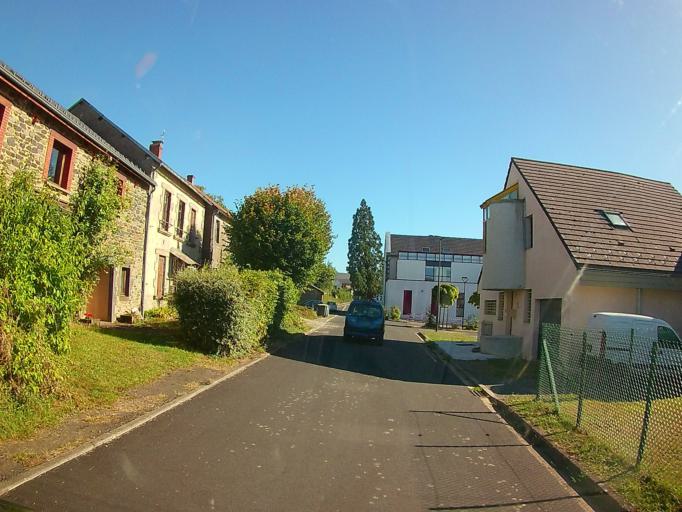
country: FR
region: Auvergne
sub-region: Departement du Puy-de-Dome
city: Chapdes-Beaufort
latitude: 45.8923
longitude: 2.8654
